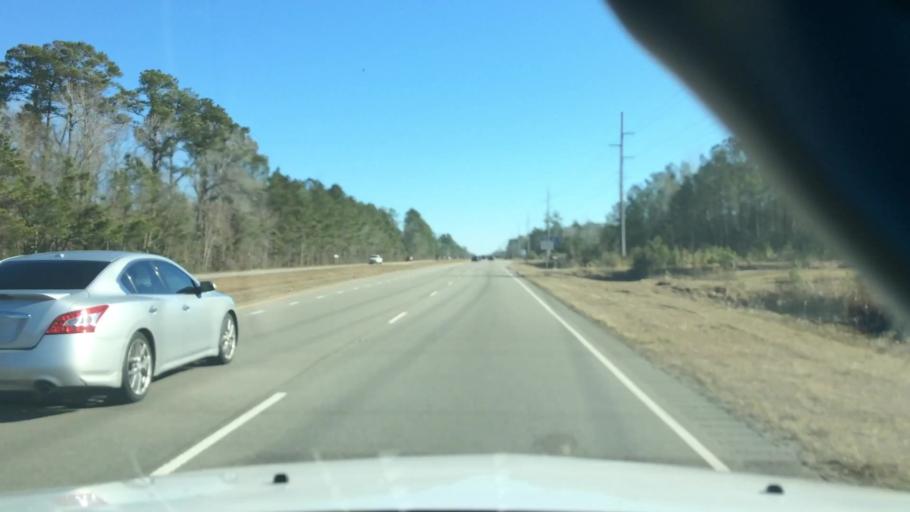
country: US
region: North Carolina
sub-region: Brunswick County
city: Shallotte
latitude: 34.0010
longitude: -78.3191
